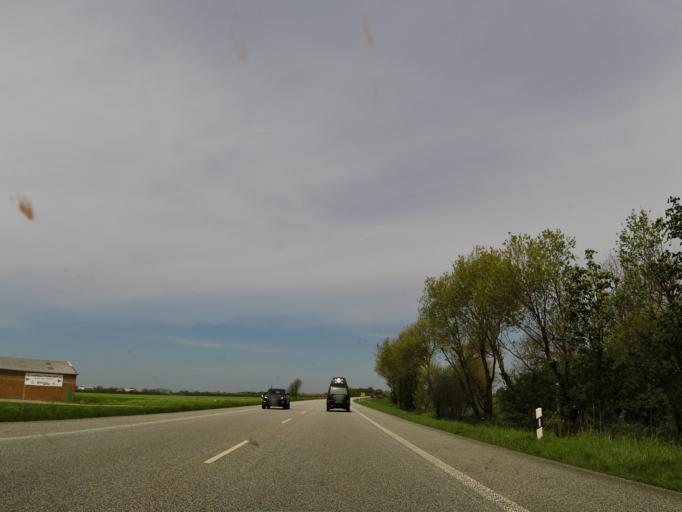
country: DE
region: Schleswig-Holstein
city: Karolinenkoog
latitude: 54.3010
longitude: 8.9656
